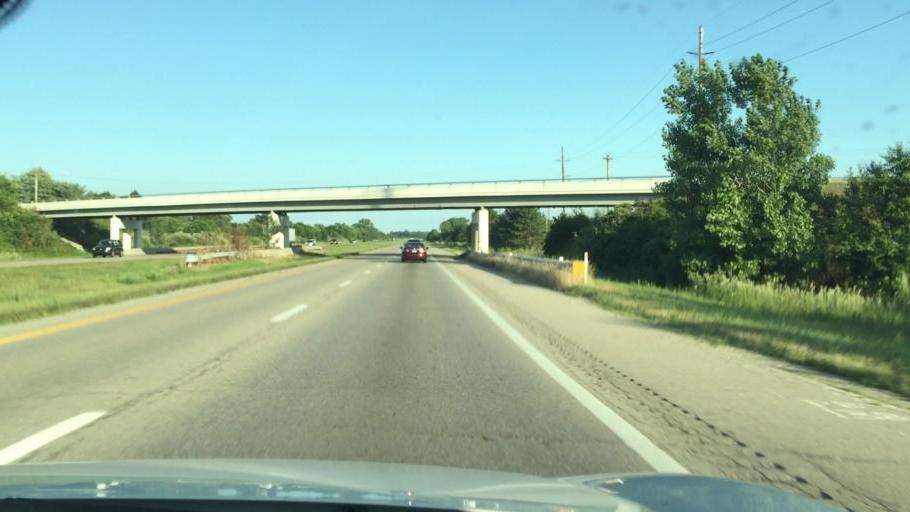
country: US
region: Ohio
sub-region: Union County
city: New California
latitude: 40.1435
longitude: -83.2094
